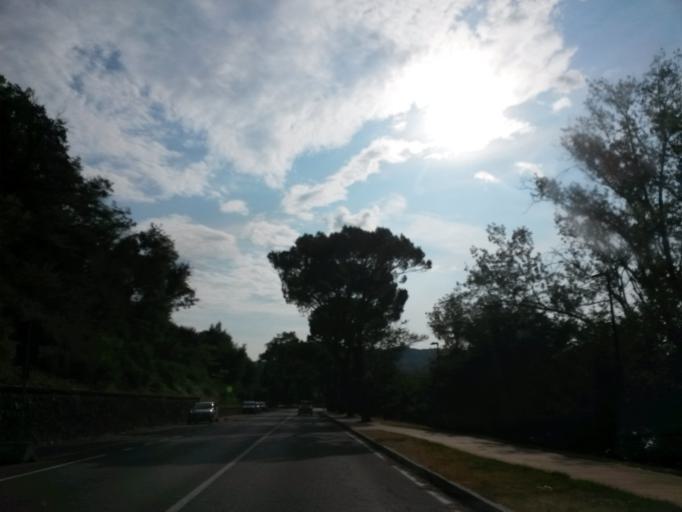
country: IT
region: Lombardy
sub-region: Provincia di Brescia
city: Padenghe sul Garda
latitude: 45.4894
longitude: 10.5265
